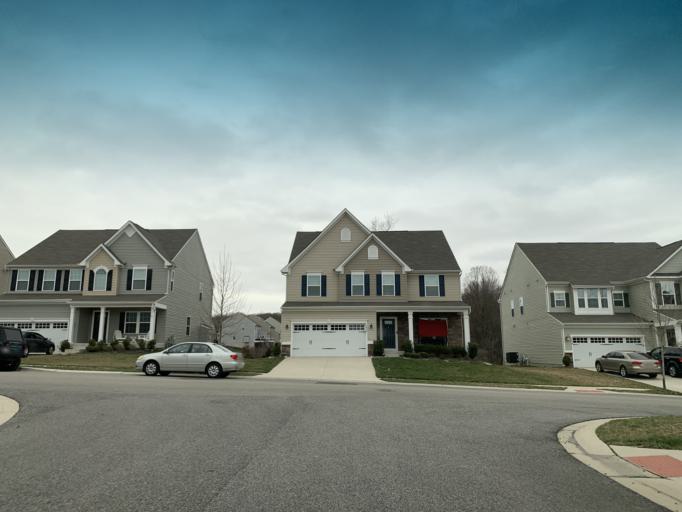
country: US
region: Maryland
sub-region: Harford County
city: Aberdeen
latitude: 39.5421
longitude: -76.1924
